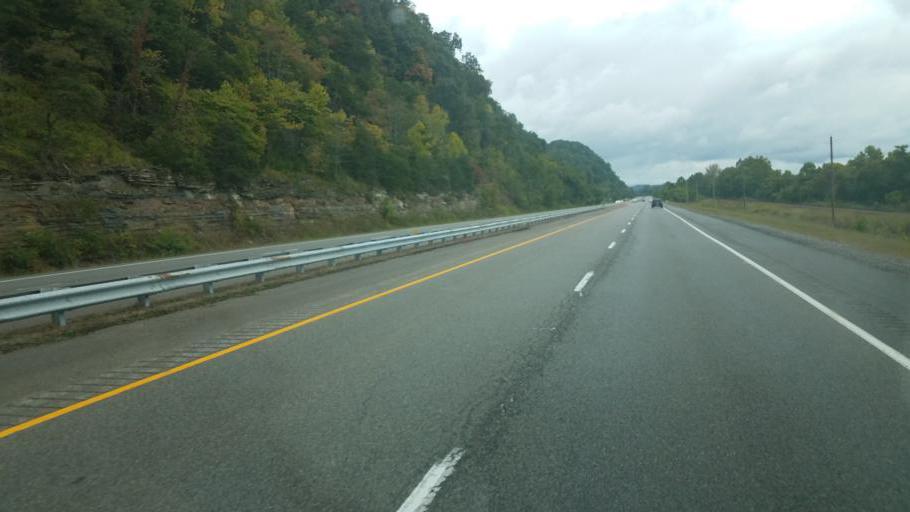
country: US
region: Ohio
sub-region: Scioto County
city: Wheelersburg
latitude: 38.6989
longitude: -82.8813
